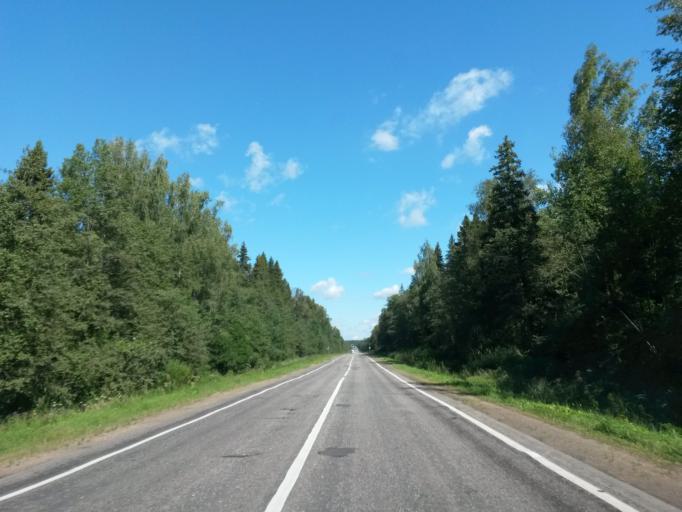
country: RU
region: Jaroslavl
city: Gavrilov-Yam
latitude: 57.4267
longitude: 39.9188
